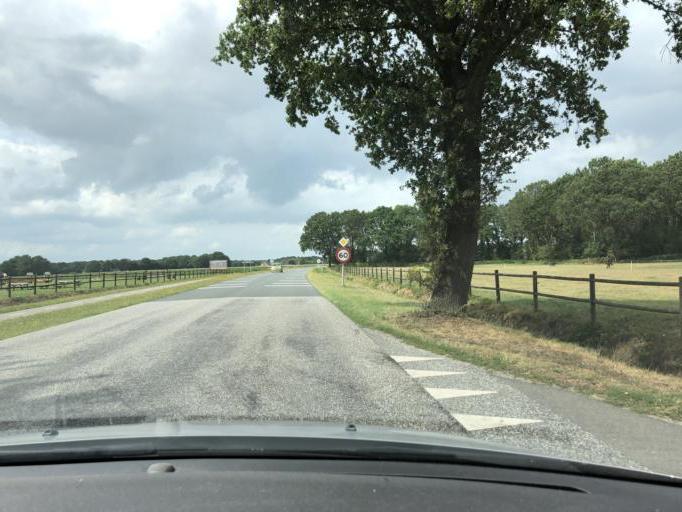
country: NL
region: Drenthe
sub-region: Gemeente Borger-Odoorn
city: Borger
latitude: 52.9253
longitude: 6.6828
